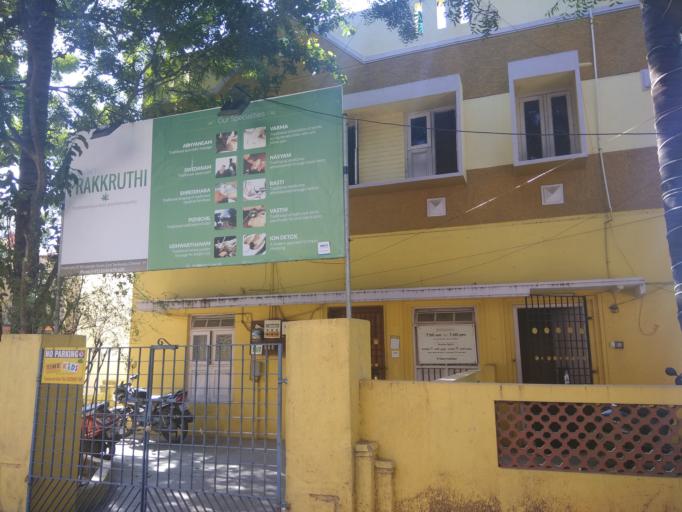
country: IN
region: Tamil Nadu
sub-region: Kancheepuram
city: Pallavaram
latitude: 12.9288
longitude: 80.1291
